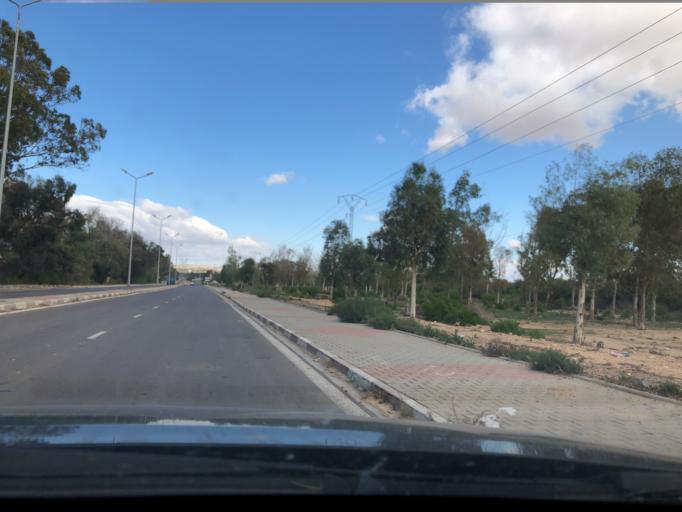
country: TN
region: Al Qasrayn
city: Kasserine
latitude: 35.1943
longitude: 8.8745
